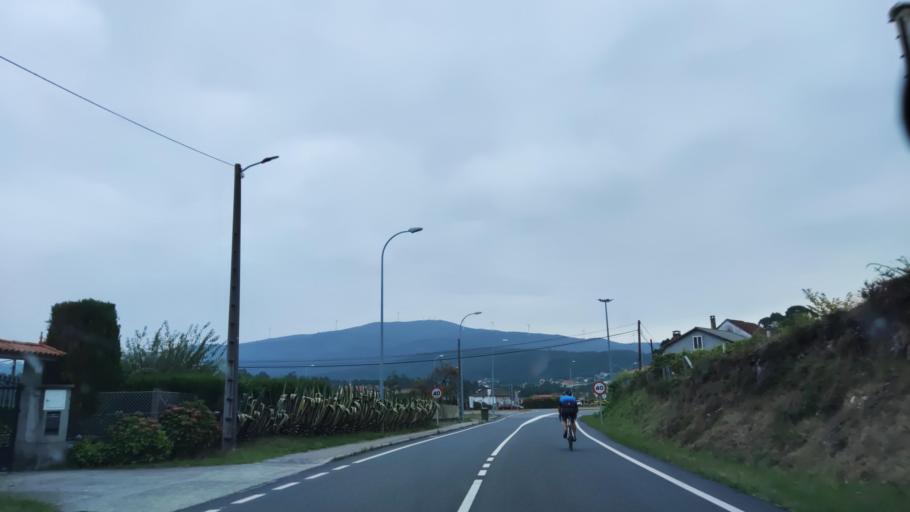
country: ES
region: Galicia
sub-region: Provincia de Pontevedra
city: Catoira
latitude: 42.6782
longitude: -8.7297
